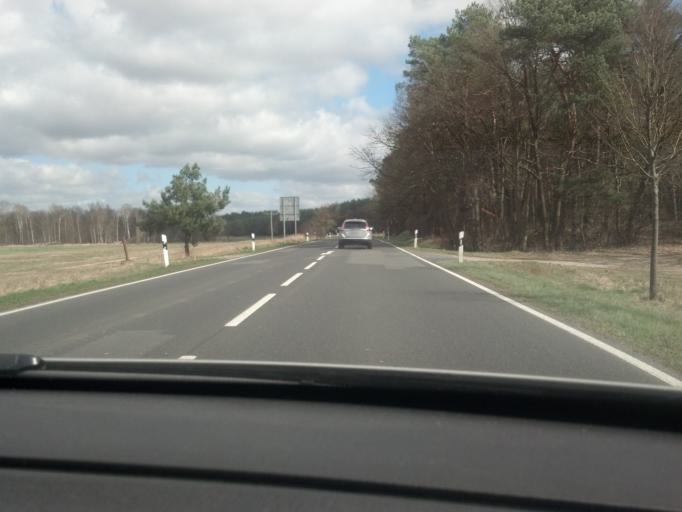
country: DE
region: Mecklenburg-Vorpommern
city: Wesenberg
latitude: 53.2930
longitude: 13.0292
